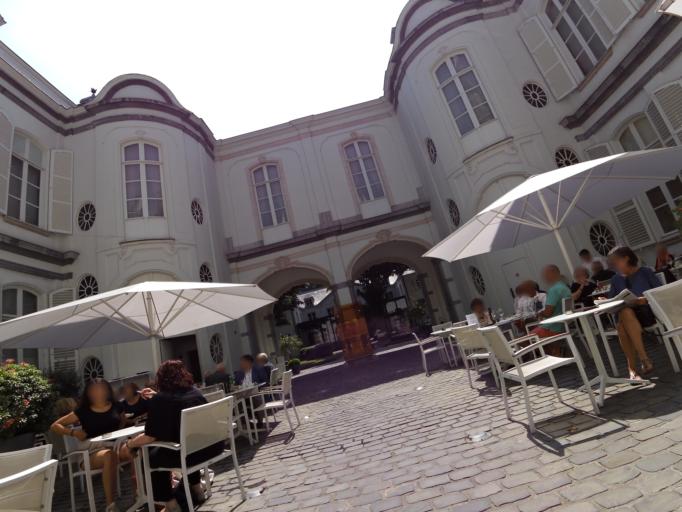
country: BE
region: Flanders
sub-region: Provincie Antwerpen
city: Antwerpen
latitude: 51.2179
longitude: 4.4084
